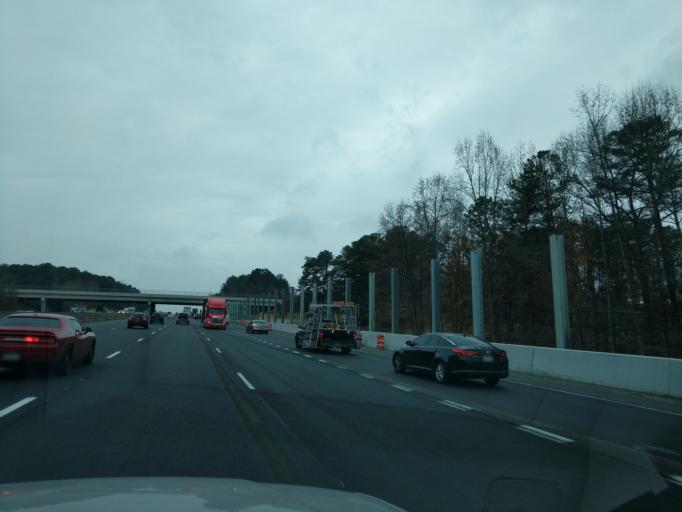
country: US
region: Georgia
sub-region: Gwinnett County
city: Suwanee
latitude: 34.0280
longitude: -84.0511
